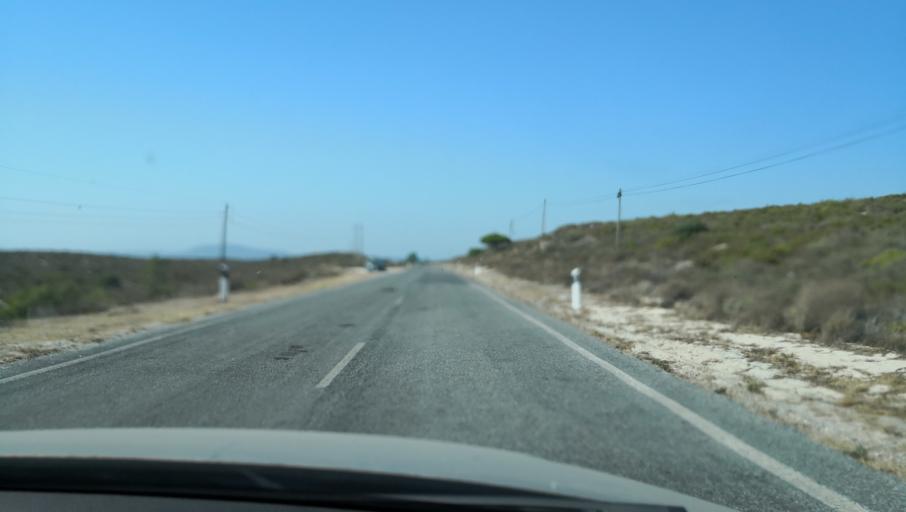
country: PT
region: Setubal
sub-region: Setubal
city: Setubal
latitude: 38.4308
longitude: -8.8269
